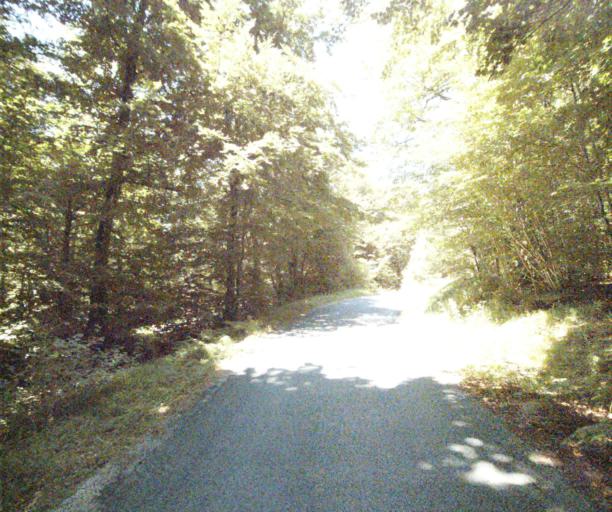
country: FR
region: Midi-Pyrenees
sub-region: Departement du Tarn
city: Dourgne
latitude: 43.4224
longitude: 2.1826
